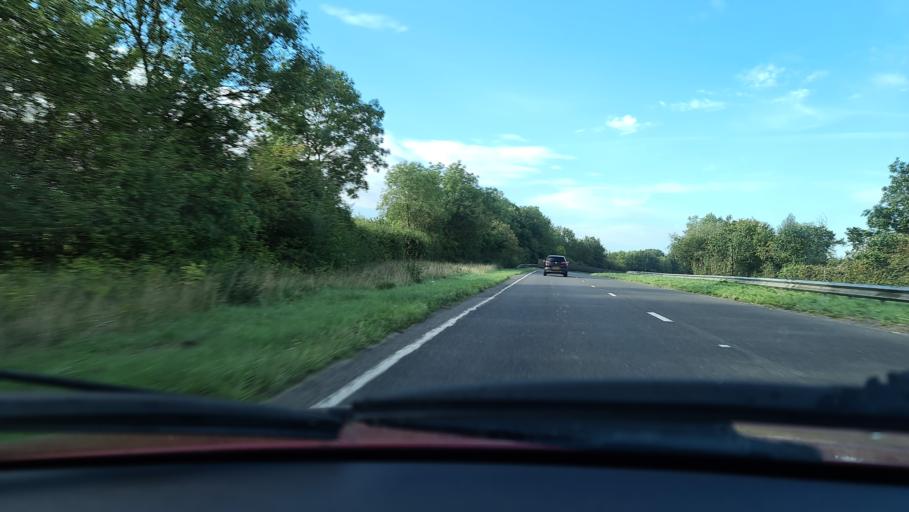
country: GB
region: England
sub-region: Oxfordshire
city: Kidlington
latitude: 51.8004
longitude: -1.2817
